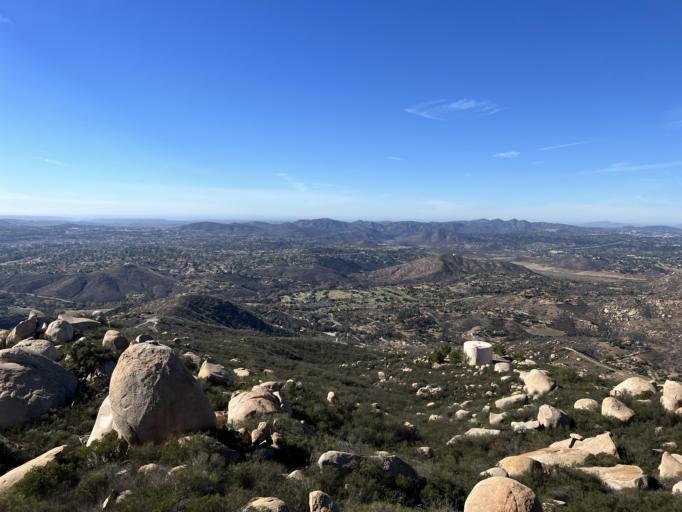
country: US
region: California
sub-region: San Diego County
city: San Pasqual
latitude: 33.0326
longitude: -116.9987
